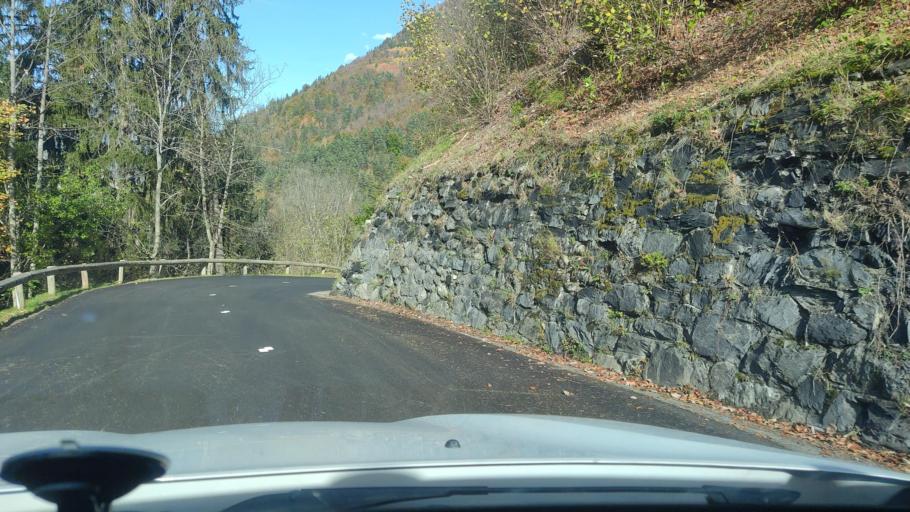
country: FR
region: Rhone-Alpes
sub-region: Departement de la Savoie
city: Saint-Jean-de-Maurienne
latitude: 45.2264
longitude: 6.3178
